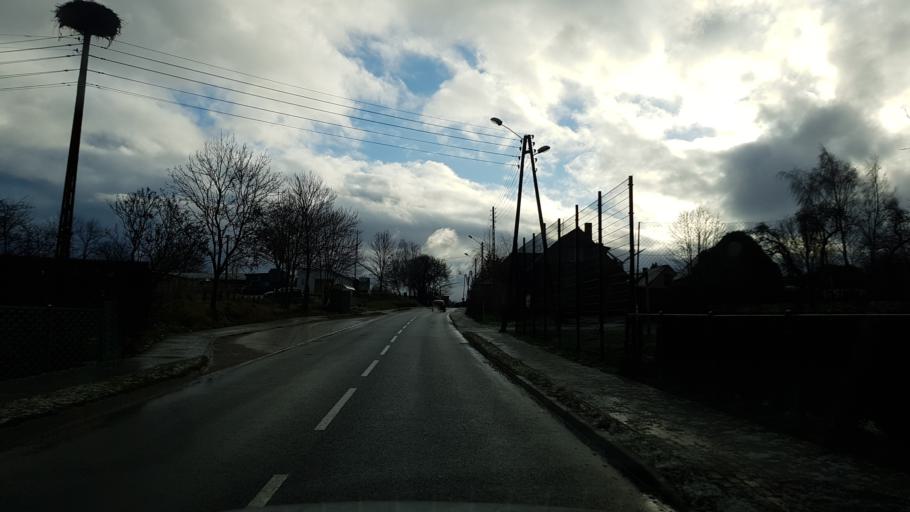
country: PL
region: West Pomeranian Voivodeship
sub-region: Powiat gryficki
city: Karnice
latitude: 54.0509
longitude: 15.0698
